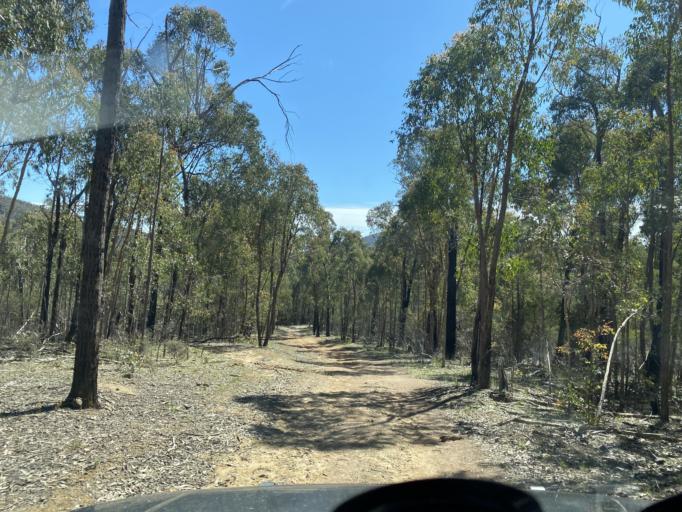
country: AU
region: Victoria
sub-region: Benalla
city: Benalla
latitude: -36.7160
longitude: 146.1812
